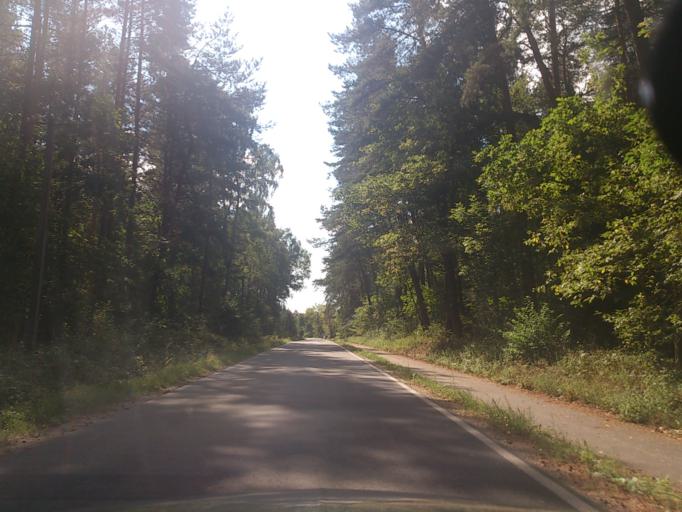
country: PL
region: Kujawsko-Pomorskie
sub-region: Powiat golubsko-dobrzynski
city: Golub-Dobrzyn
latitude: 53.0803
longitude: 19.0308
